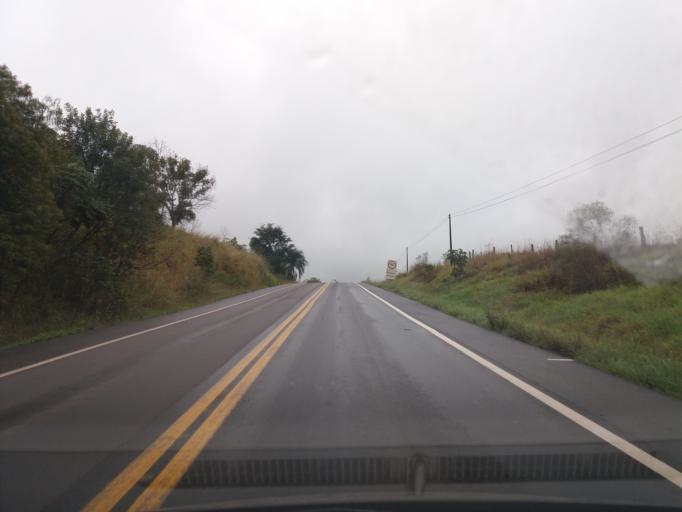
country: BR
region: Parana
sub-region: Realeza
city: Realeza
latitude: -25.5708
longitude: -53.5708
